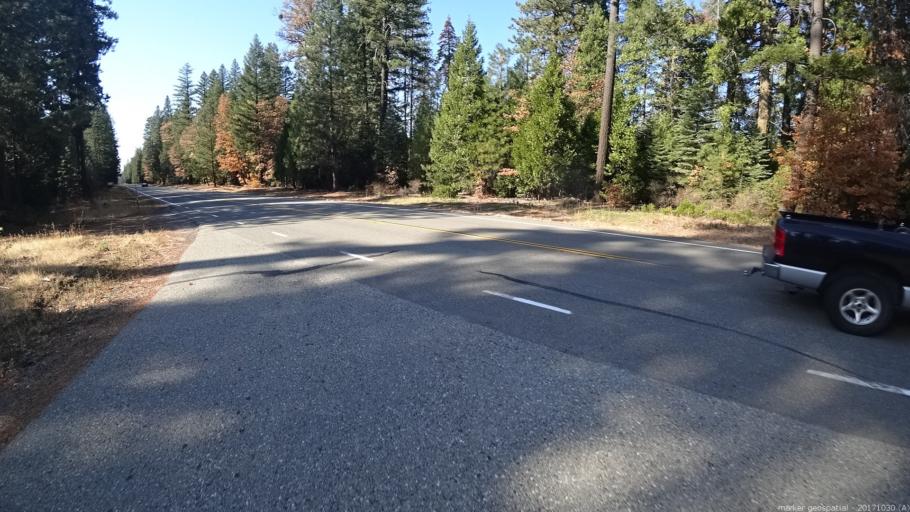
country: US
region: California
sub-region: Shasta County
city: Shingletown
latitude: 40.5172
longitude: -121.7297
